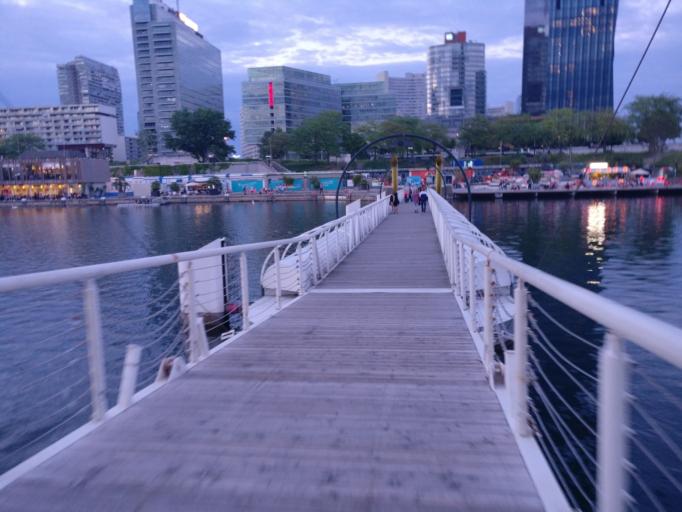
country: AT
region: Vienna
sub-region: Wien Stadt
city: Vienna
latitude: 48.2308
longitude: 16.4094
